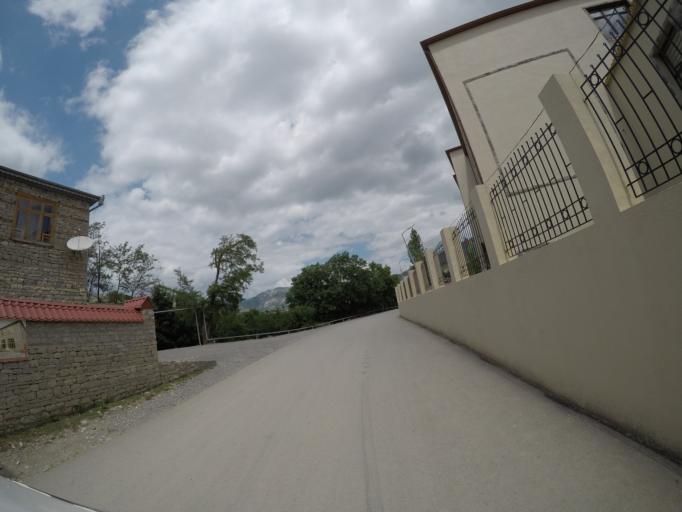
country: AZ
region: Ismayilli
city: Basqal
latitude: 40.8491
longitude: 48.3867
